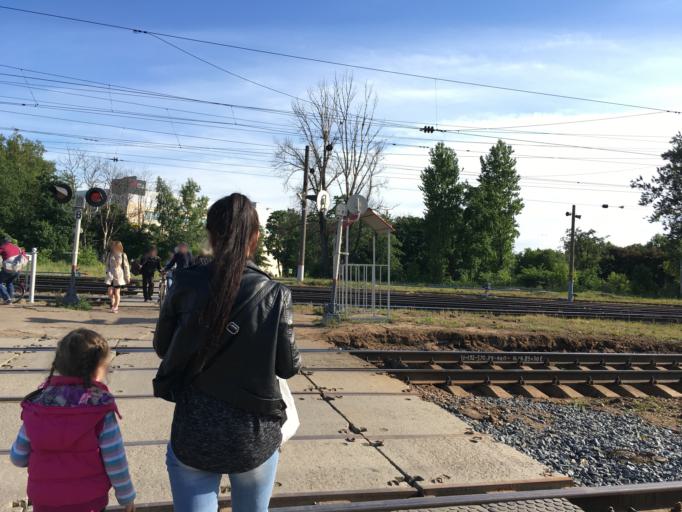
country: RU
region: Leningrad
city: Sampsonievskiy
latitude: 59.9905
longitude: 30.3524
